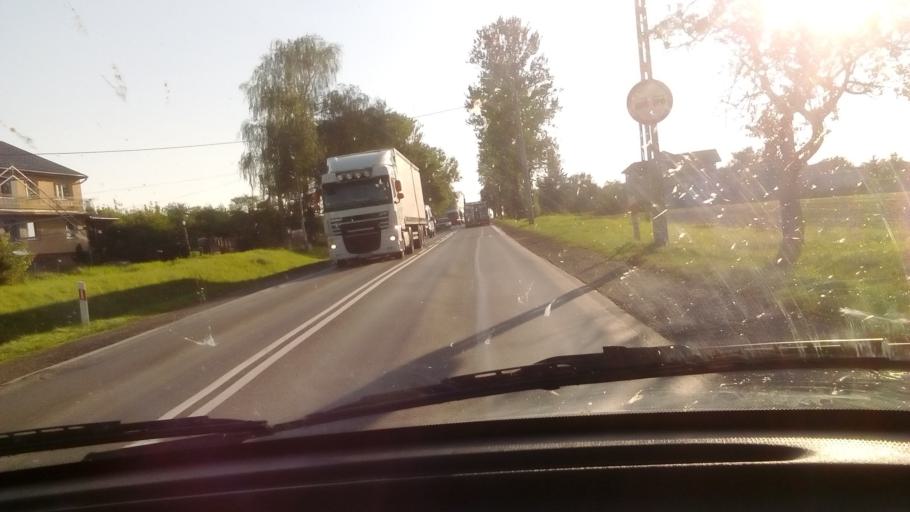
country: PL
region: Podlasie
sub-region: Powiat grajewski
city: Grajewo
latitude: 53.6409
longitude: 22.4411
